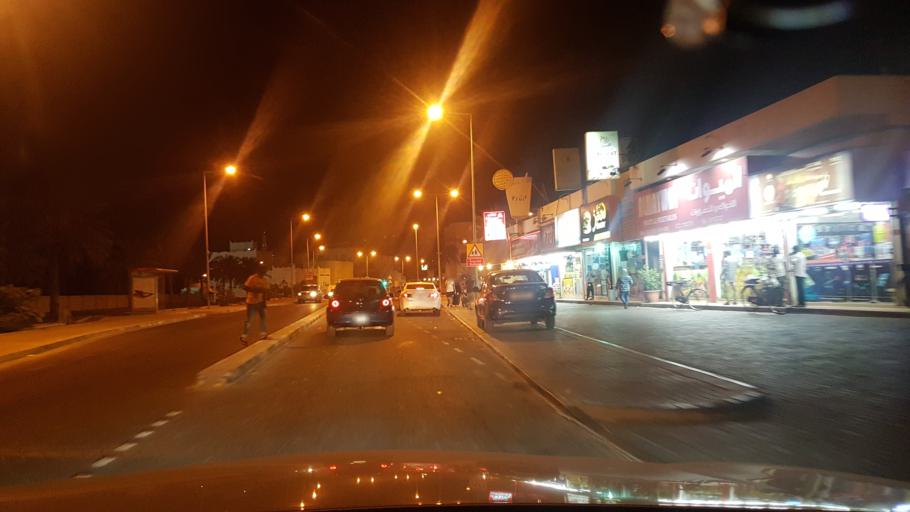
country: BH
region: Central Governorate
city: Dar Kulayb
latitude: 26.0505
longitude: 50.4879
